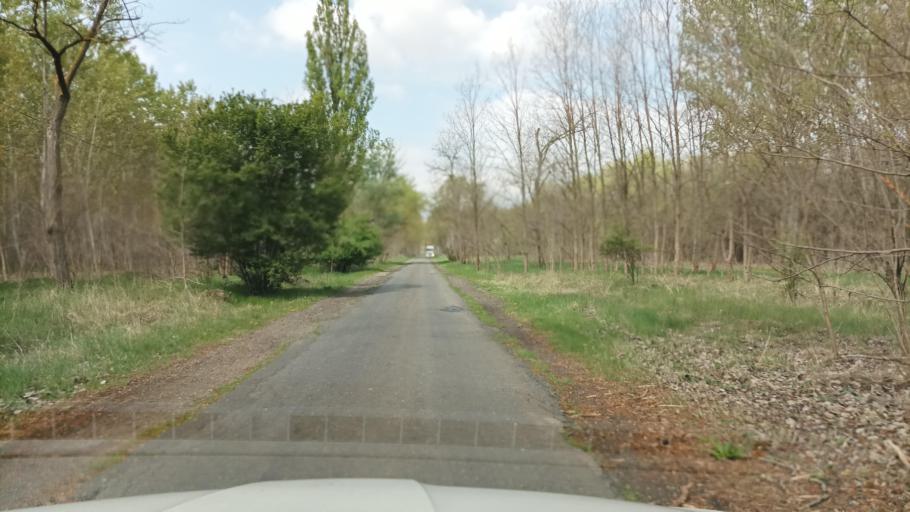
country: HU
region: Pest
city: Kocser
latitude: 47.0470
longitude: 19.9215
